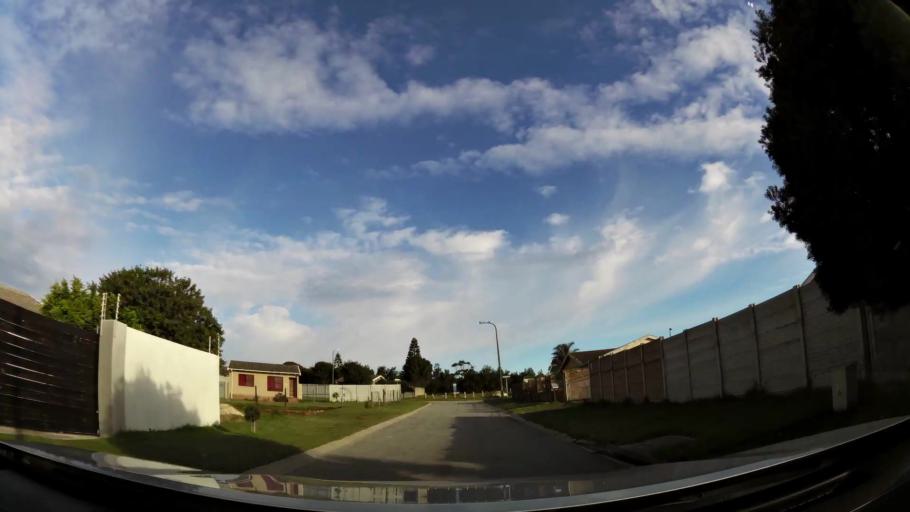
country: ZA
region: Eastern Cape
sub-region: Nelson Mandela Bay Metropolitan Municipality
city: Port Elizabeth
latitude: -33.9641
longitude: 25.4736
